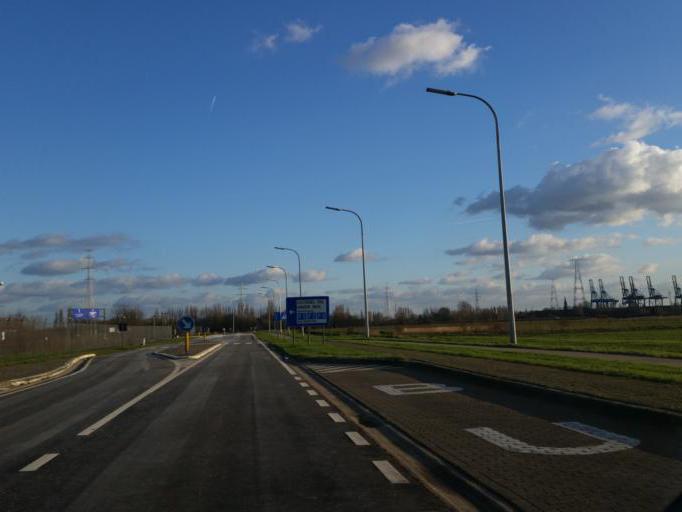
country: BE
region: Flanders
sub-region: Provincie Oost-Vlaanderen
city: Beveren
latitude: 51.3199
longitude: 4.2536
